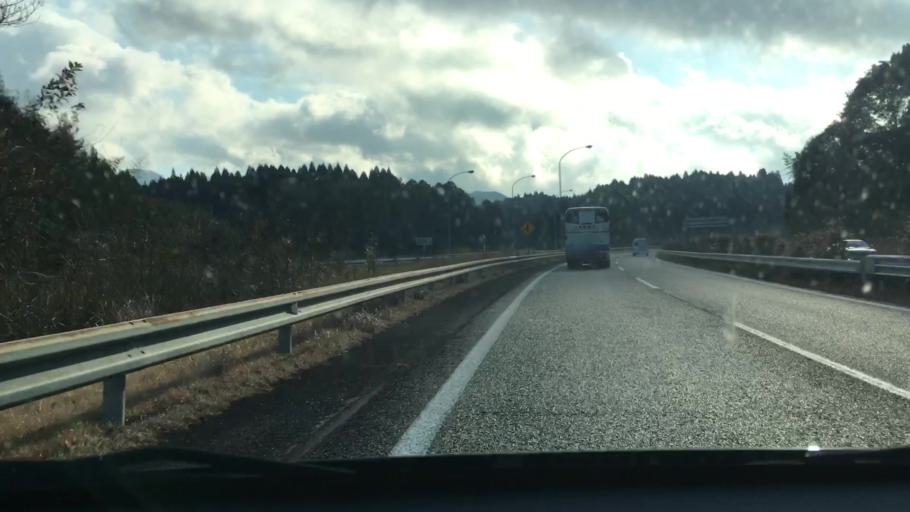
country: JP
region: Kagoshima
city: Okuchi-shinohara
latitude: 32.0292
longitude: 130.7971
